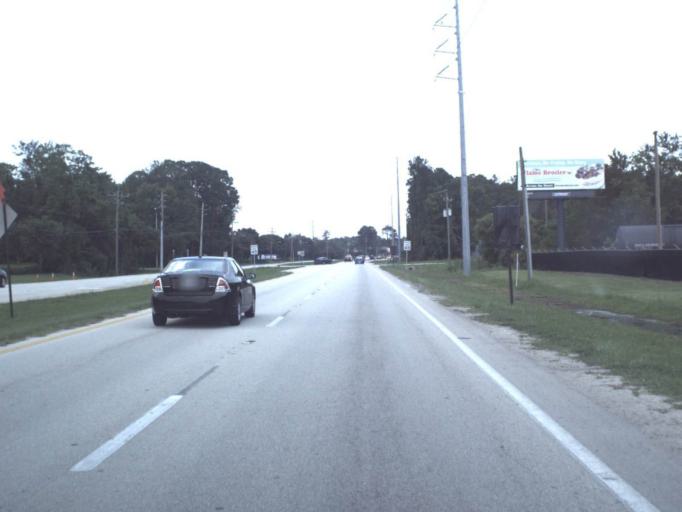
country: US
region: Florida
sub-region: Duval County
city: Jacksonville
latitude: 30.2426
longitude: -81.5991
